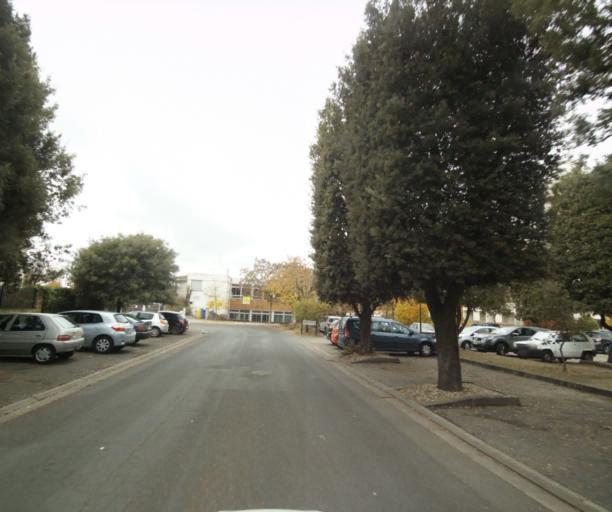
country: FR
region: Poitou-Charentes
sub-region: Departement de la Charente-Maritime
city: Saintes
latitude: 45.7348
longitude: -0.6511
